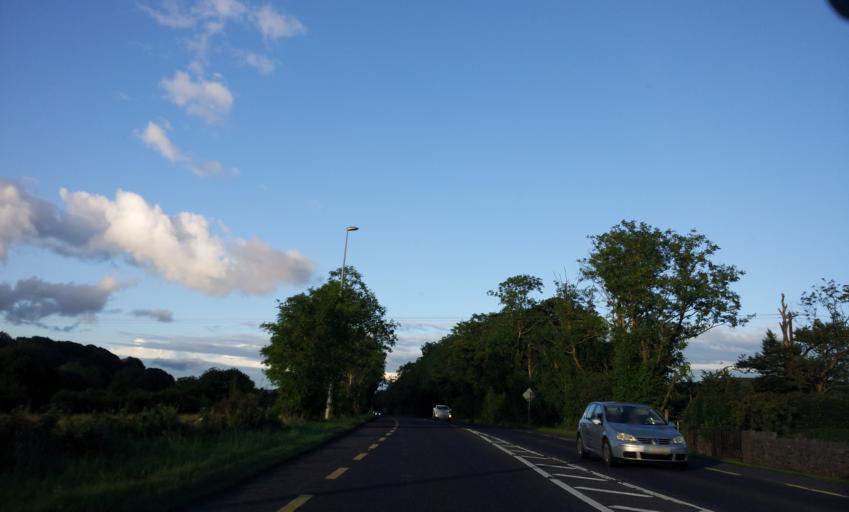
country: IE
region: Munster
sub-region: County Limerick
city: Abbeyfeale
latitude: 52.3830
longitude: -9.2163
